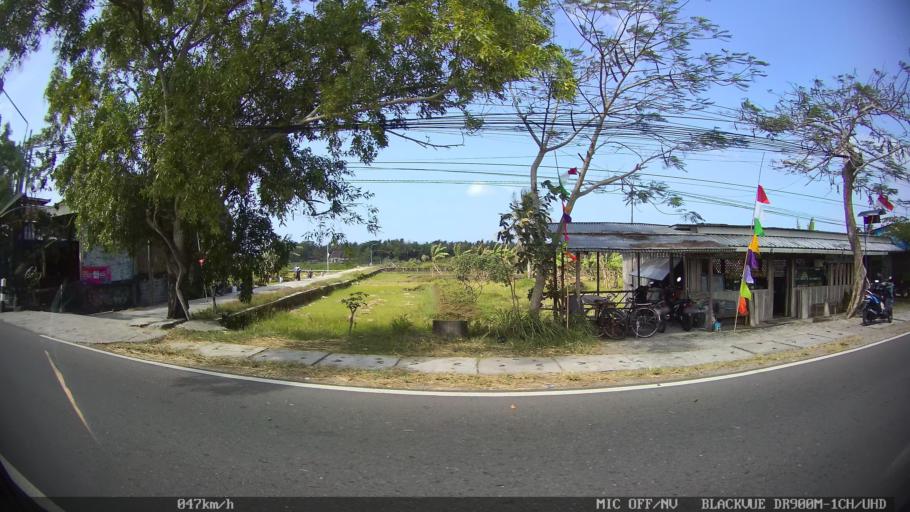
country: ID
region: Daerah Istimewa Yogyakarta
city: Srandakan
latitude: -7.8948
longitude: 110.1487
